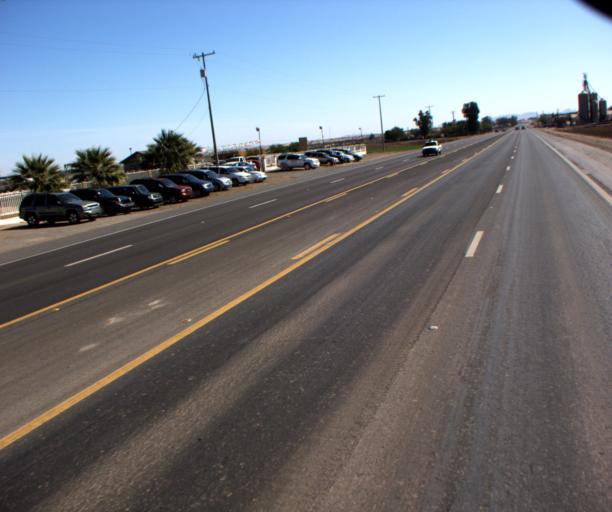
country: US
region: Arizona
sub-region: Yuma County
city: Somerton
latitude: 32.5967
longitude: -114.6917
